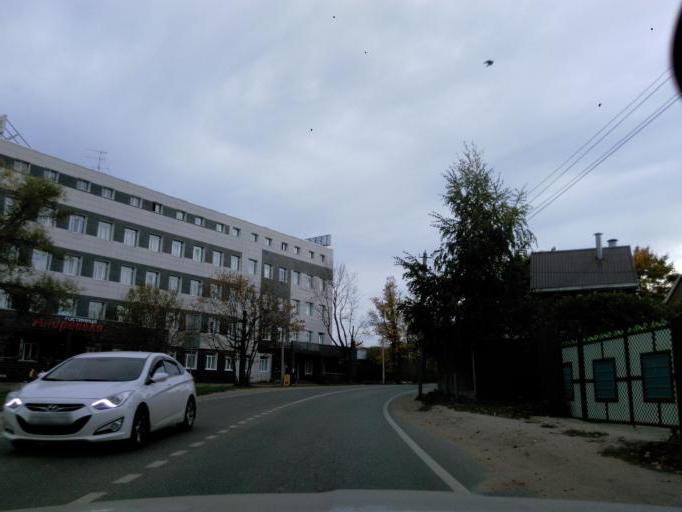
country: RU
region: Moskovskaya
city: Andreyevka
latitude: 55.9818
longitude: 37.1370
